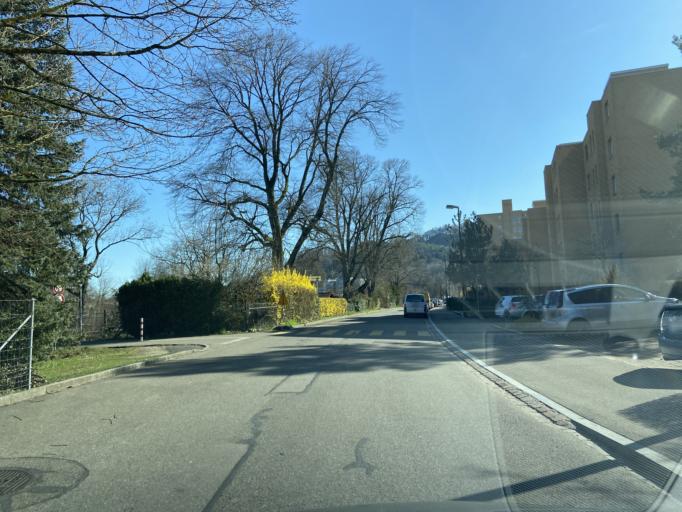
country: CH
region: Zurich
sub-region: Bezirk Winterthur
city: Wuelflingen (Kreis 6)
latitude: 47.5105
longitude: 8.6825
